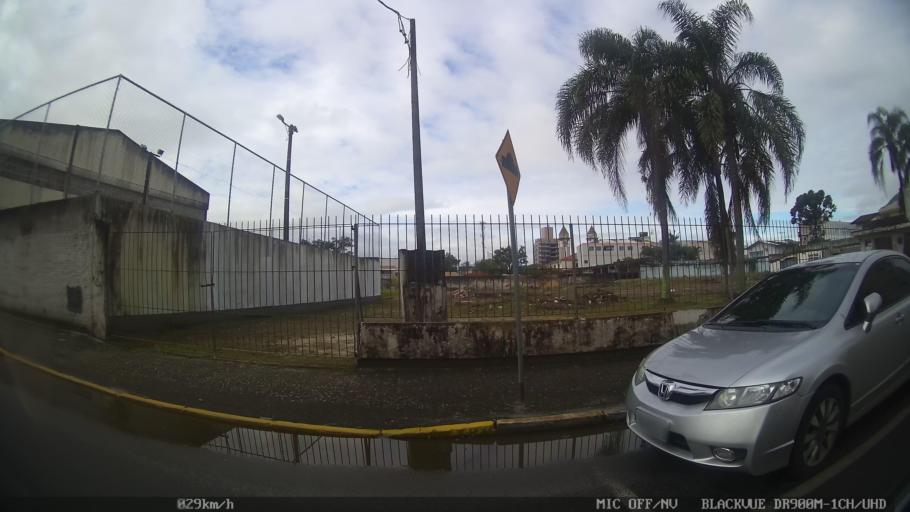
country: BR
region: Santa Catarina
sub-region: Biguacu
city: Biguacu
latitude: -27.4935
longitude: -48.6554
